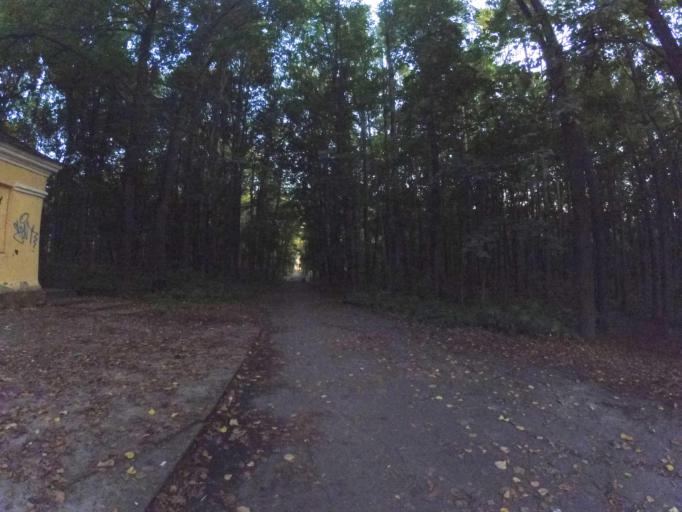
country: RU
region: Moscow
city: Strogino
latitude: 55.8512
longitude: 37.3986
